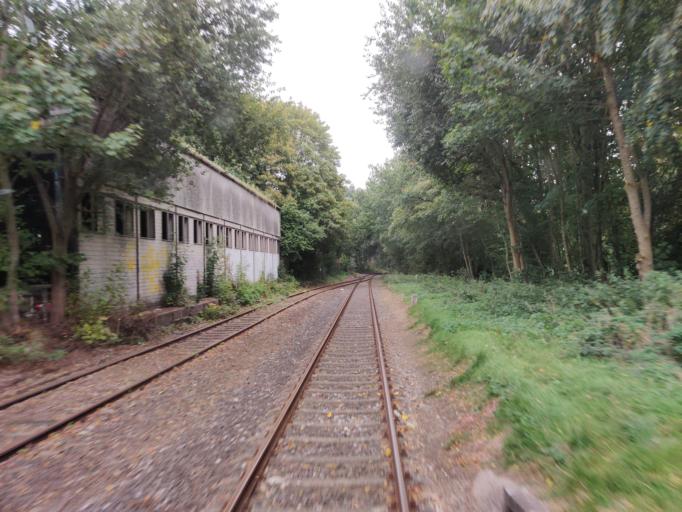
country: DE
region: Lower Saxony
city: Osterholz-Scharmbeck
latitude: 53.2334
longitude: 8.8184
